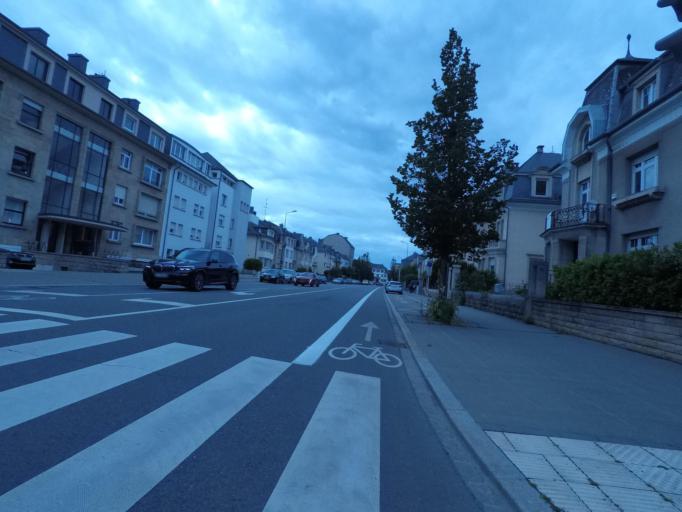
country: LU
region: Luxembourg
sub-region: Canton de Luxembourg
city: Luxembourg
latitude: 49.6074
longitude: 6.1149
